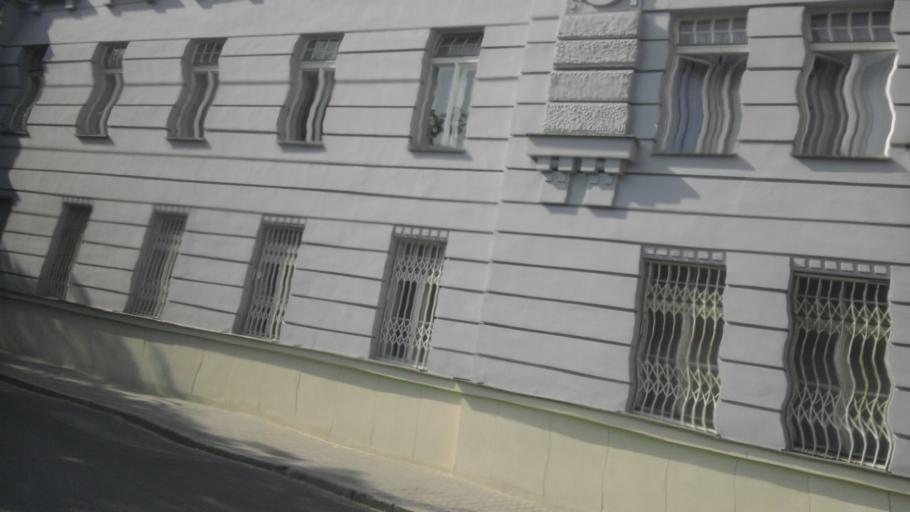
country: SK
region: Bratislavsky
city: Bratislava
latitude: 48.1408
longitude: 17.1164
